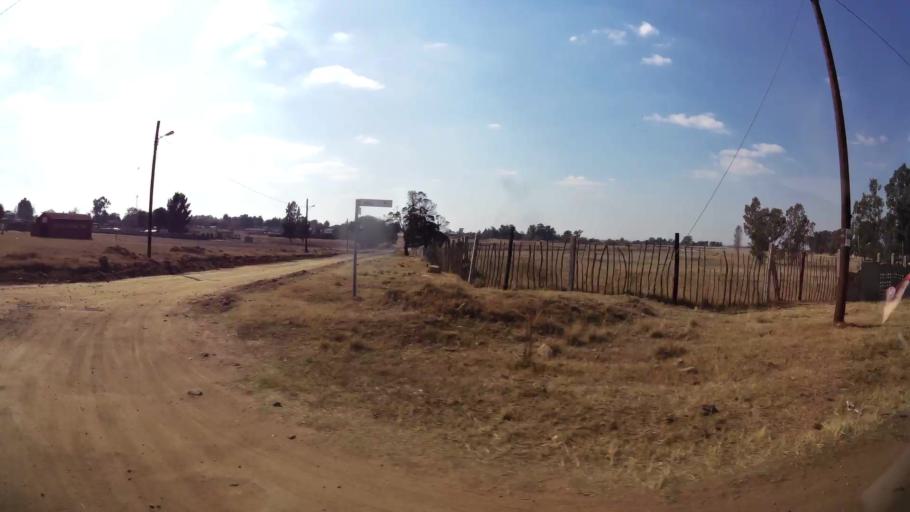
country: ZA
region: Gauteng
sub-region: Ekurhuleni Metropolitan Municipality
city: Benoni
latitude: -26.1118
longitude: 28.4020
